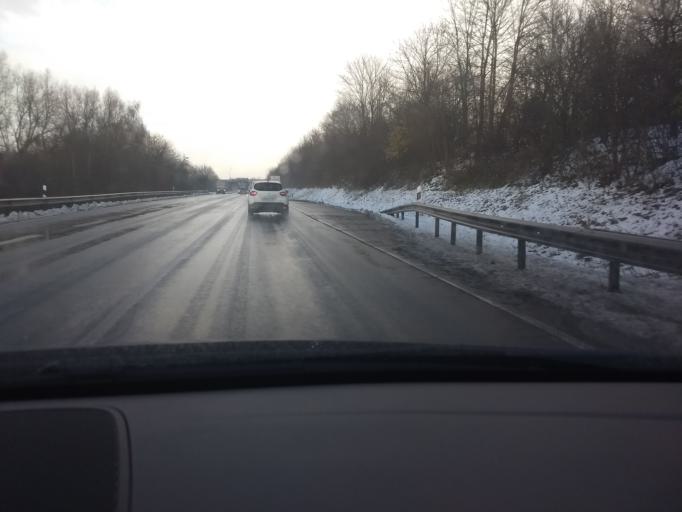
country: DE
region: Lower Saxony
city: Nordhorn
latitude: 52.4272
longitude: 7.0861
